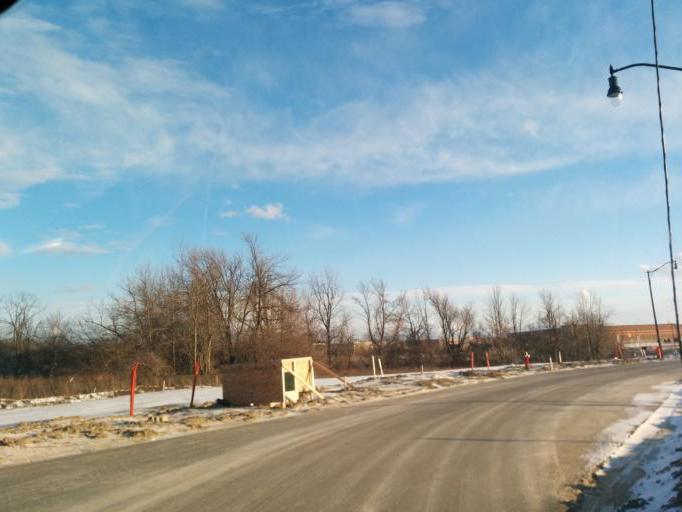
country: CA
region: Ontario
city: Brampton
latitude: 43.6626
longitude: -79.8168
